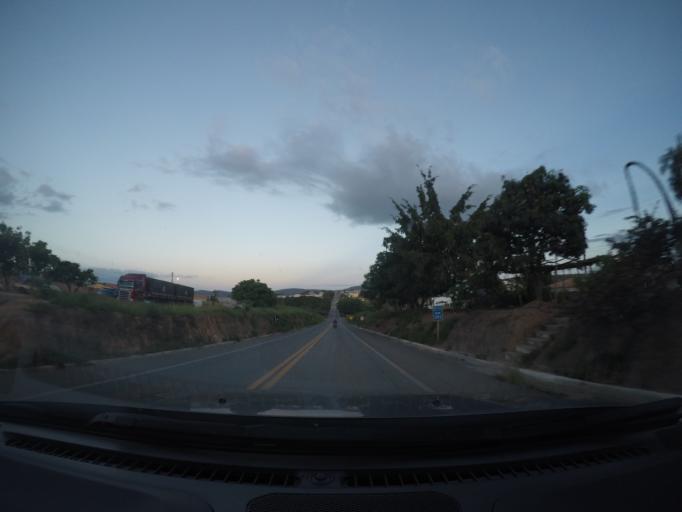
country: BR
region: Bahia
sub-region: Seabra
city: Seabra
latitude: -12.4286
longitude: -41.7789
